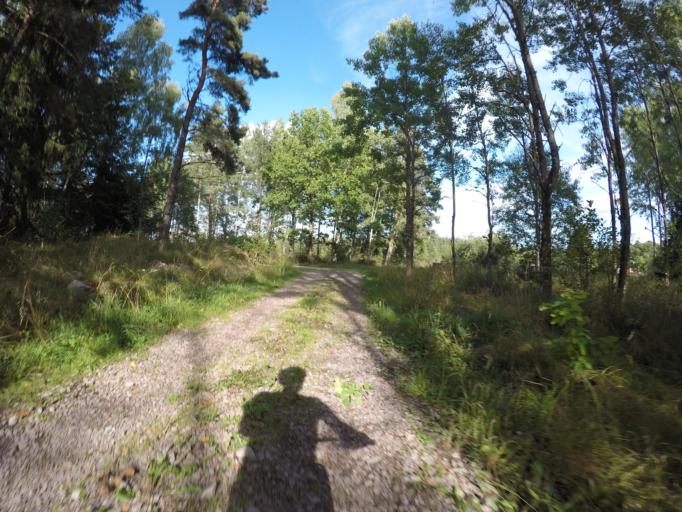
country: SE
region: Soedermanland
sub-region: Eskilstuna Kommun
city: Kvicksund
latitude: 59.5320
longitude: 16.3346
